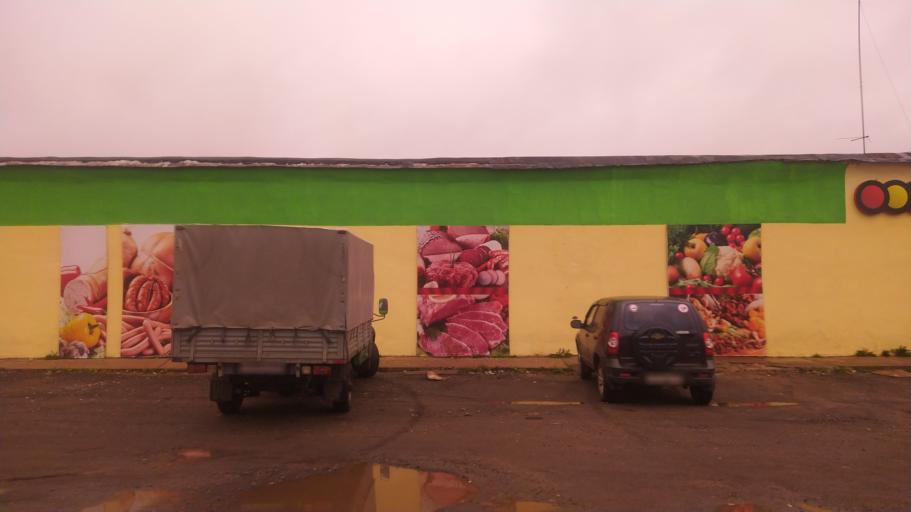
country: RU
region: Tverskaya
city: Tver
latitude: 56.8274
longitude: 35.9178
